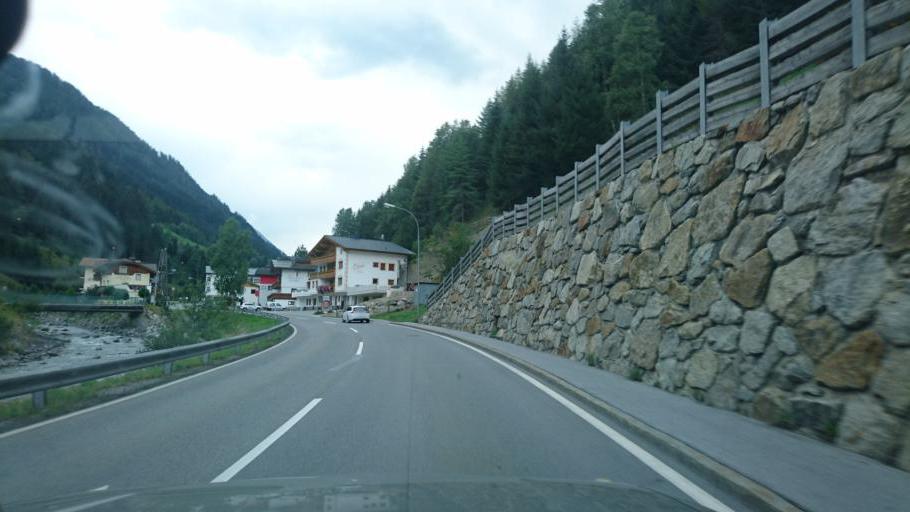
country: AT
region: Tyrol
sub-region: Politischer Bezirk Landeck
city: Kappl
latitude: 47.0490
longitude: 10.3457
